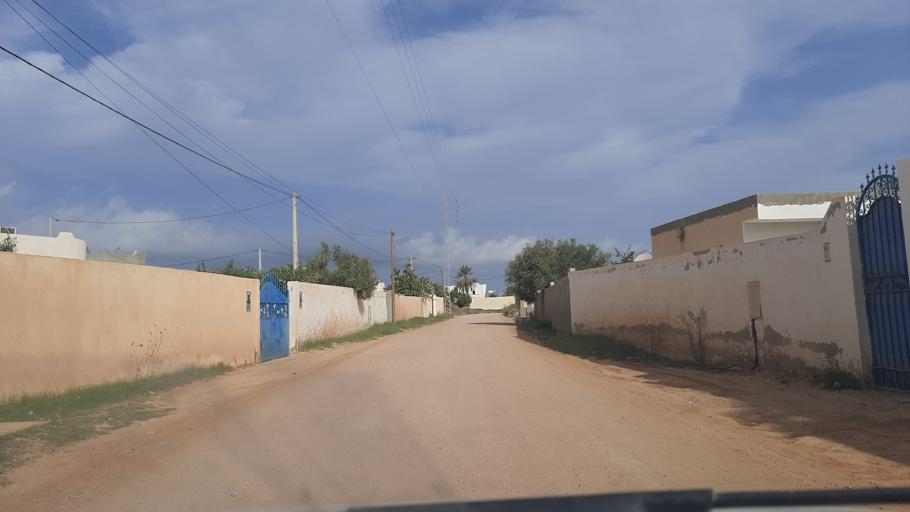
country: TN
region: Madanin
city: Midoun
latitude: 33.8142
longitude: 11.0251
